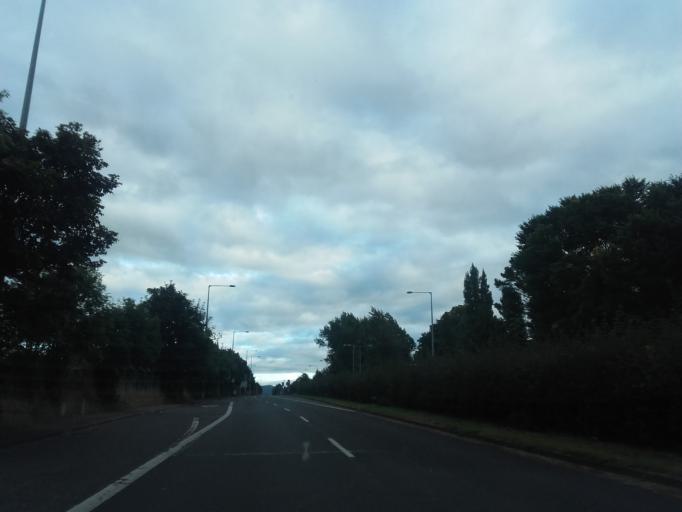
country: IE
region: Leinster
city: Tallaght
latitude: 53.3046
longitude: -6.3798
